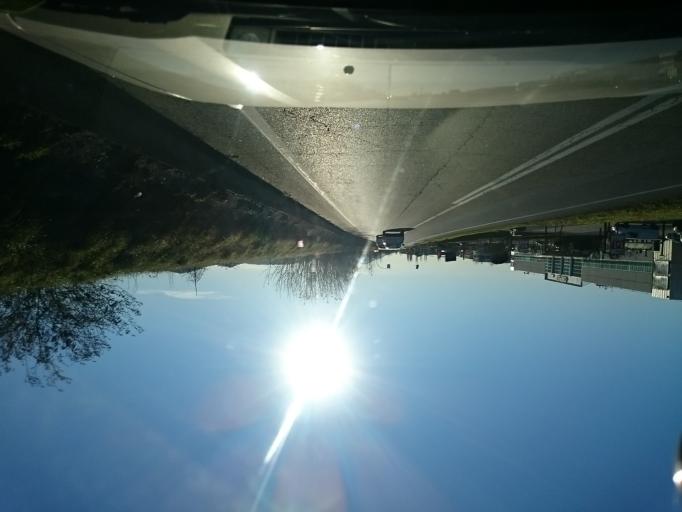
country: IT
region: Veneto
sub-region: Provincia di Padova
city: Terradura
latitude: 45.3295
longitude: 11.8167
